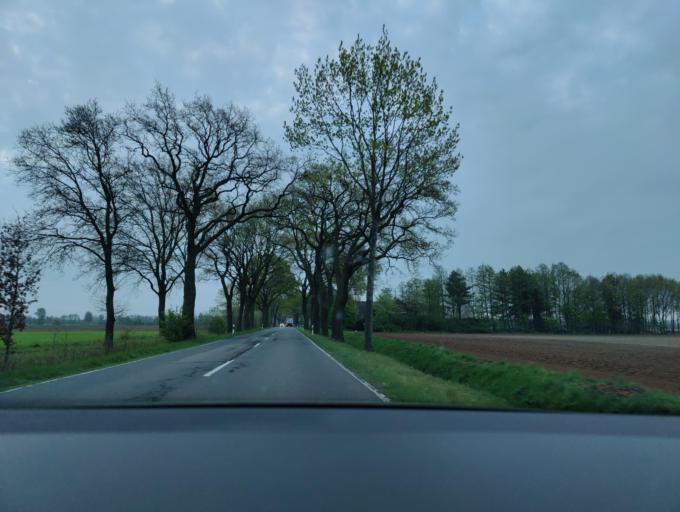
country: DE
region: Lower Saxony
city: Wietmarschen
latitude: 52.5086
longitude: 7.1616
